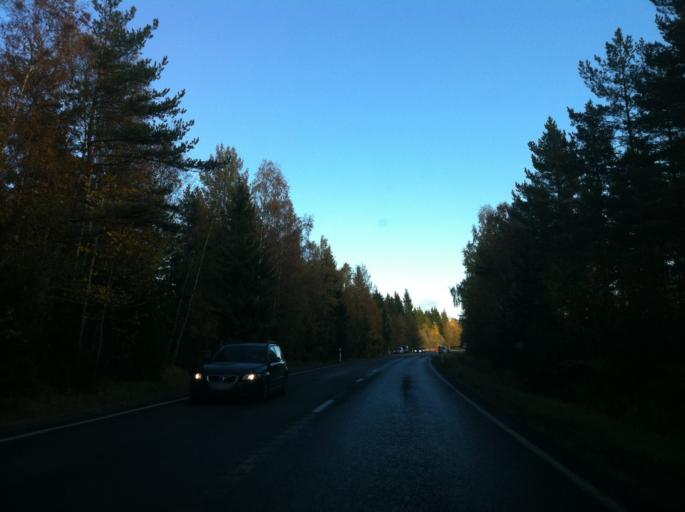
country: SE
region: Uppsala
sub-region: Osthammars Kommun
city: Oregrund
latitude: 60.3310
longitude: 18.3820
